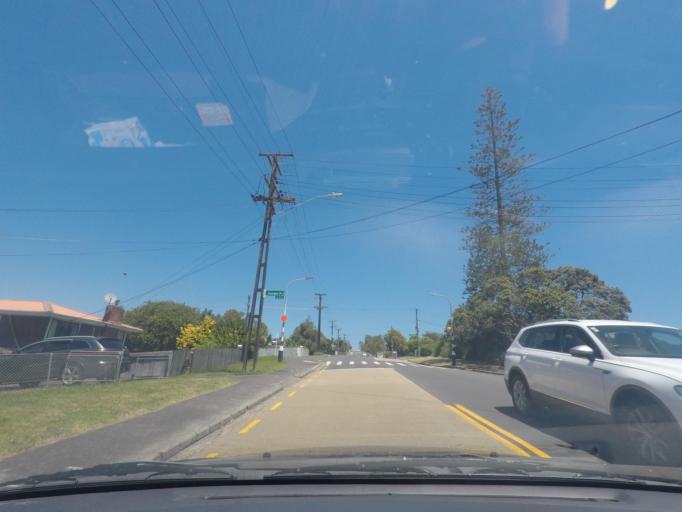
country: NZ
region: Auckland
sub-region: Auckland
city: Waitakere
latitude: -36.9152
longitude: 174.7157
